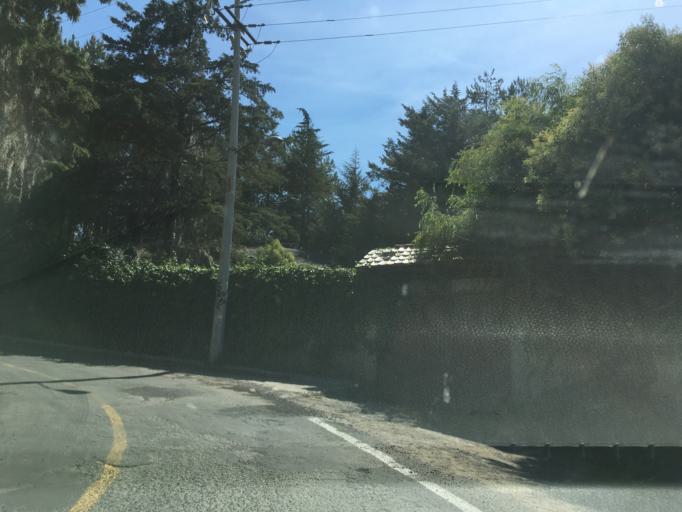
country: MX
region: Hidalgo
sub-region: Omitlan de Juarez
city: San Antonio el Paso
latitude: 20.2219
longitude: -98.5605
